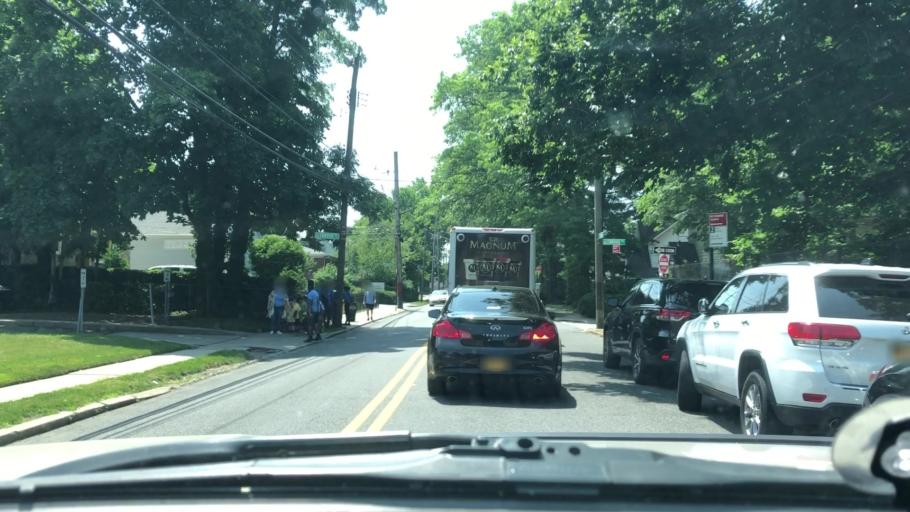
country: US
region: New Jersey
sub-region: Hudson County
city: Bayonne
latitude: 40.6249
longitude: -74.1142
